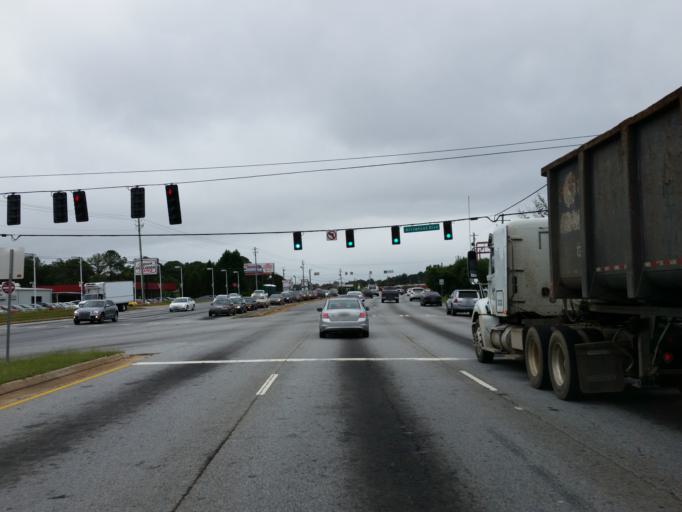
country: US
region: Georgia
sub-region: Clayton County
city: Morrow
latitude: 33.5790
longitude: -84.3743
